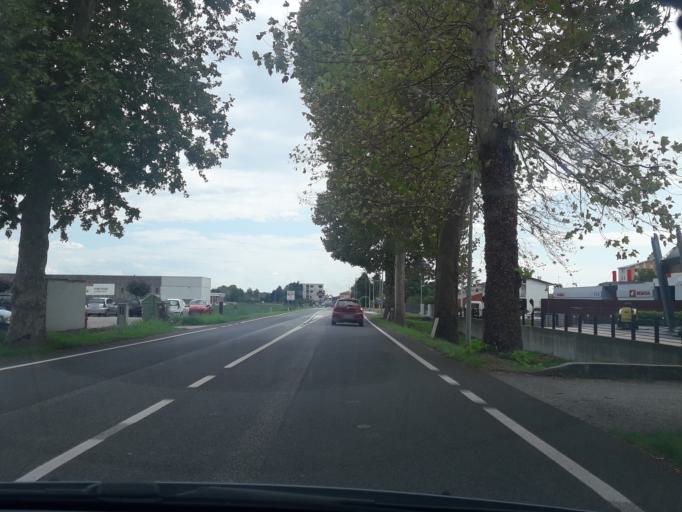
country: IT
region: Friuli Venezia Giulia
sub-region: Provincia di Udine
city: Udine
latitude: 46.0263
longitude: 13.2594
